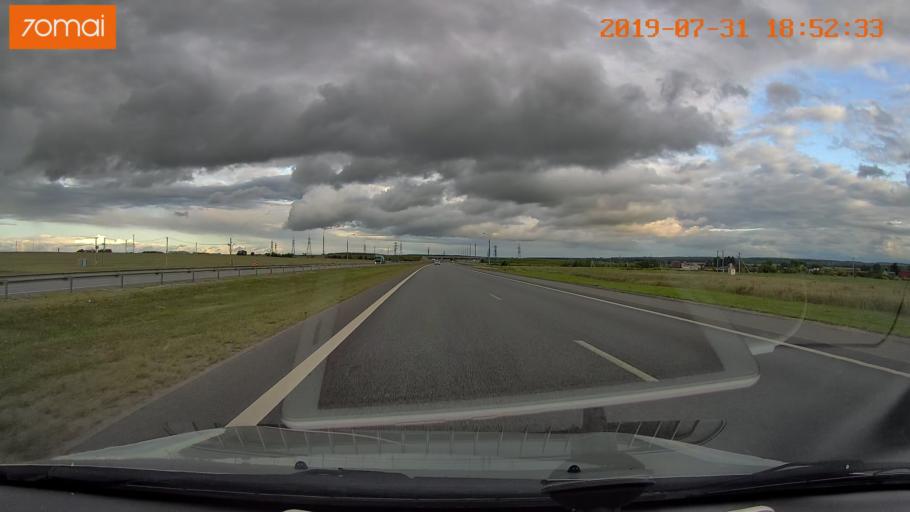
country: RU
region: Moskovskaya
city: Voskresensk
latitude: 55.2127
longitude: 38.6346
